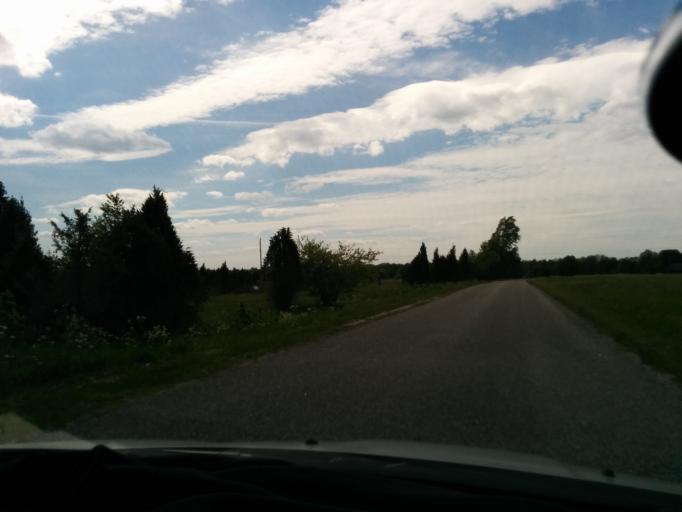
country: EE
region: Harju
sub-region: Loksa linn
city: Loksa
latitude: 59.5376
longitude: 25.8250
